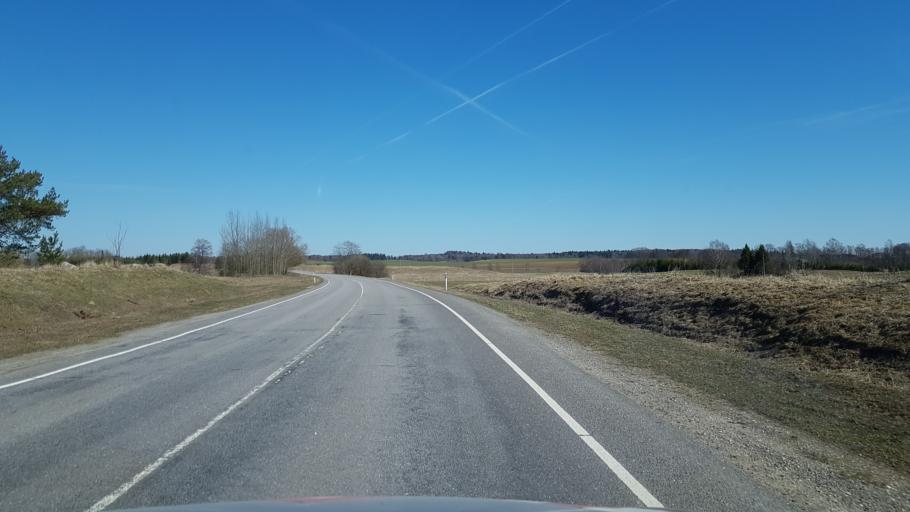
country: EE
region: Laeaene-Virumaa
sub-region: Vinni vald
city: Vinni
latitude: 59.3144
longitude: 26.4521
